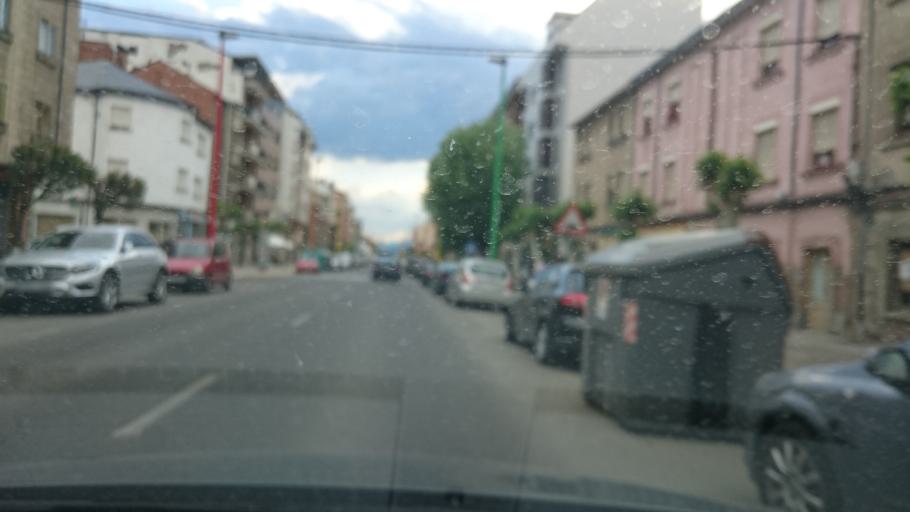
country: ES
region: Castille and Leon
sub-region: Provincia de Leon
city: Ponferrada
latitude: 42.5449
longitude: -6.6164
